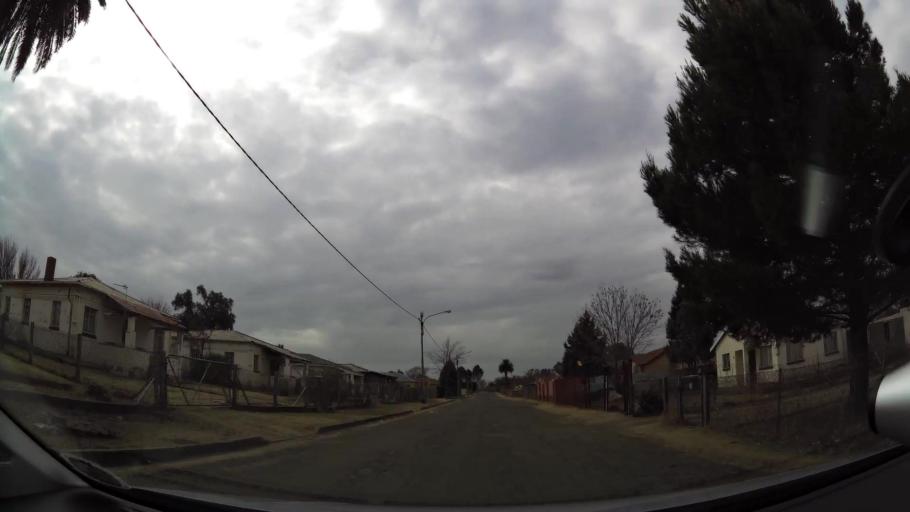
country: ZA
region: Orange Free State
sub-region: Fezile Dabi District Municipality
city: Kroonstad
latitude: -27.6551
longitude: 27.2374
